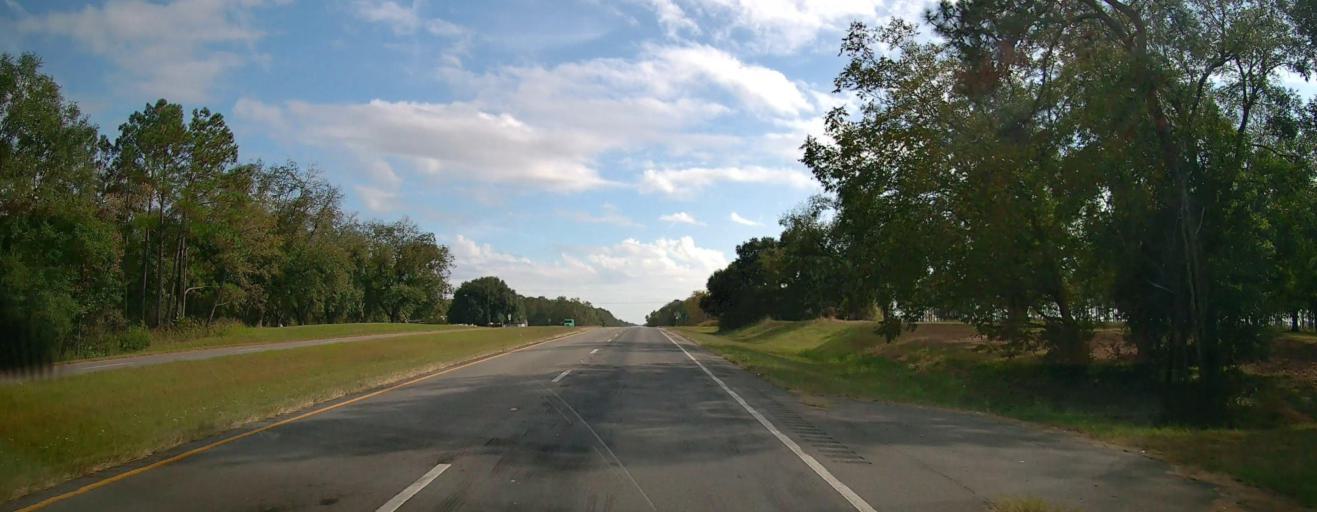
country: US
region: Georgia
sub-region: Thomas County
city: Meigs
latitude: 31.0113
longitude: -84.0533
